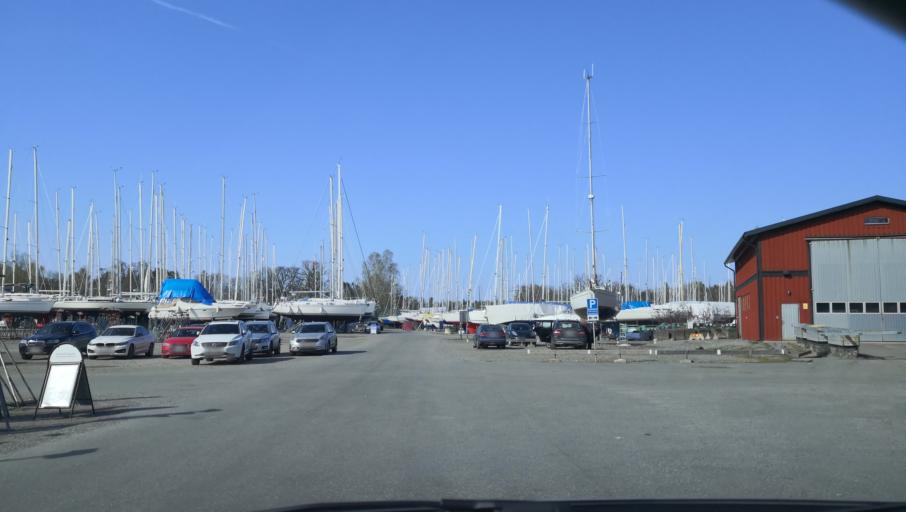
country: SE
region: Stockholm
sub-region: Varmdo Kommun
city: Holo
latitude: 59.2997
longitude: 18.6507
